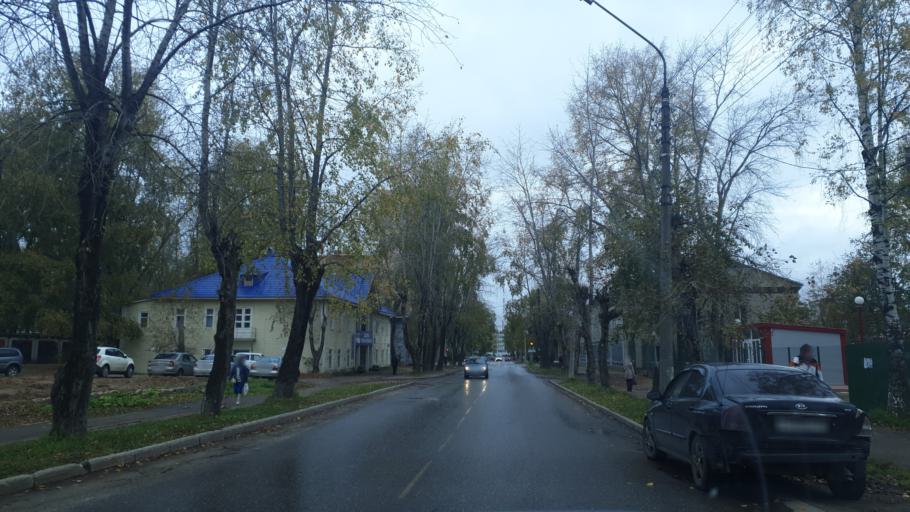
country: RU
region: Komi Republic
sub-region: Syktyvdinskiy Rayon
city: Syktyvkar
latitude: 61.6704
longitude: 50.8174
